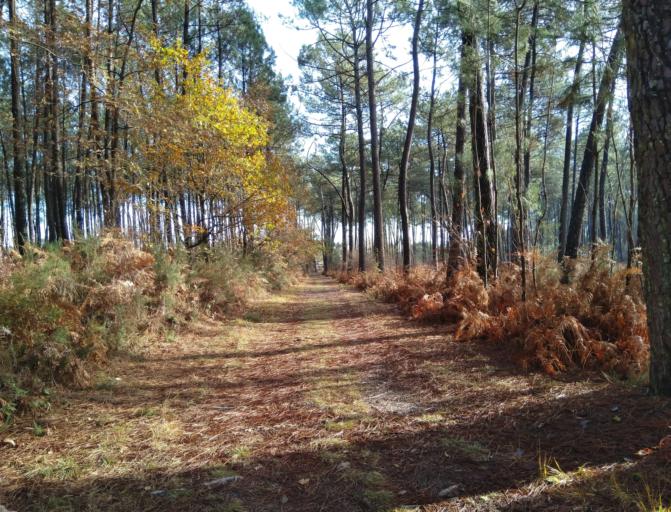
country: FR
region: Aquitaine
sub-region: Departement des Landes
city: Mees
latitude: 43.7057
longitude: -1.1234
